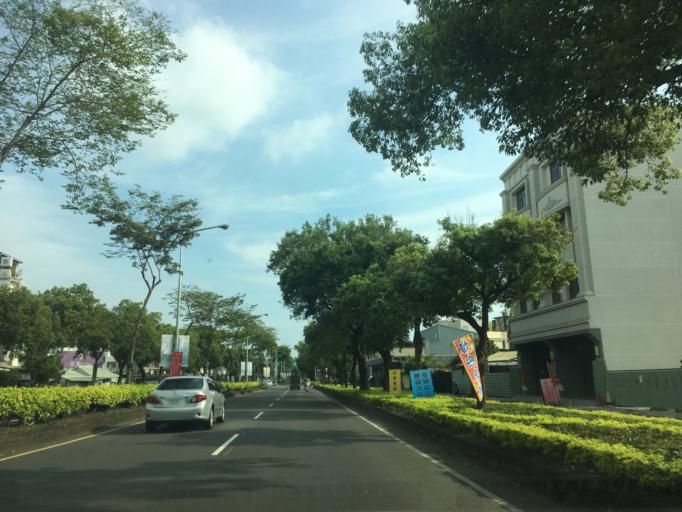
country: TW
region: Taiwan
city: Zhongxing New Village
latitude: 23.9821
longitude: 120.6813
